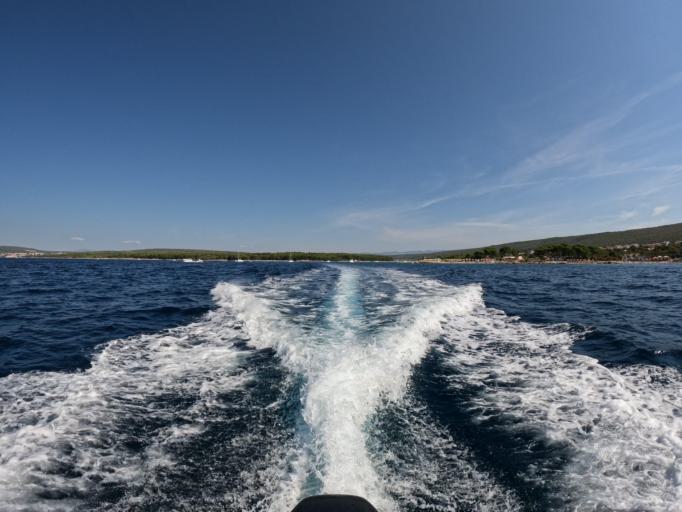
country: HR
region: Primorsko-Goranska
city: Punat
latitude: 45.0063
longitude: 14.6206
